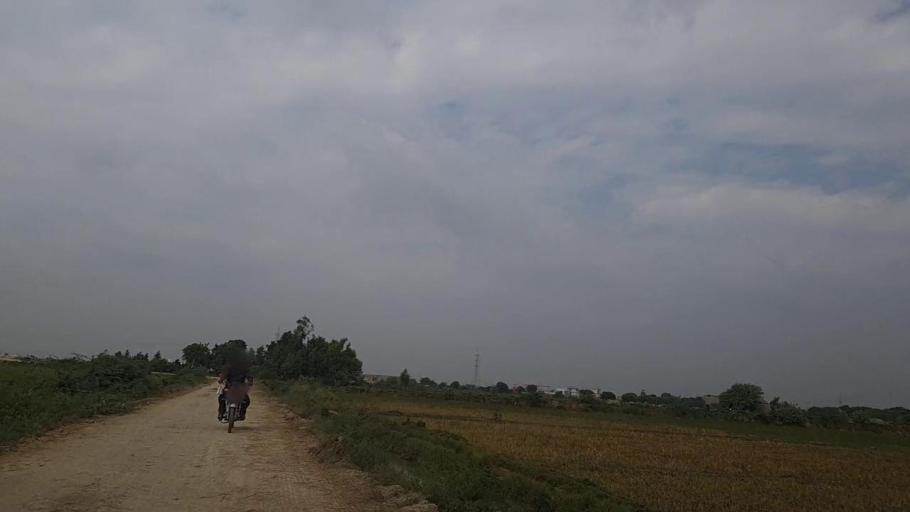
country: PK
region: Sindh
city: Daro Mehar
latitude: 24.6089
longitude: 68.0938
